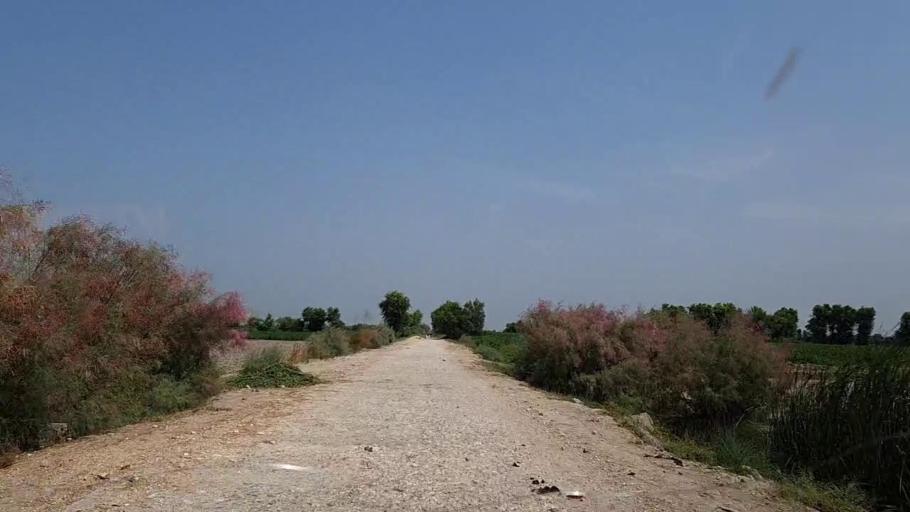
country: PK
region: Sindh
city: Adilpur
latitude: 27.8409
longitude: 69.2757
